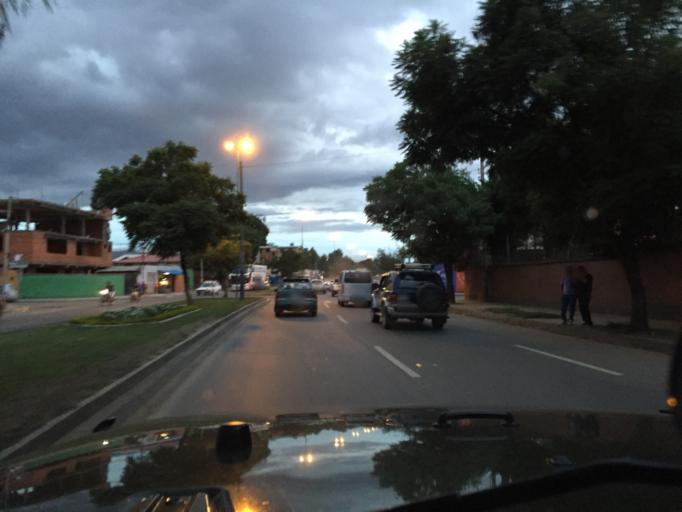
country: BO
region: Cochabamba
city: Cochabamba
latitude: -17.4068
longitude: -66.1765
